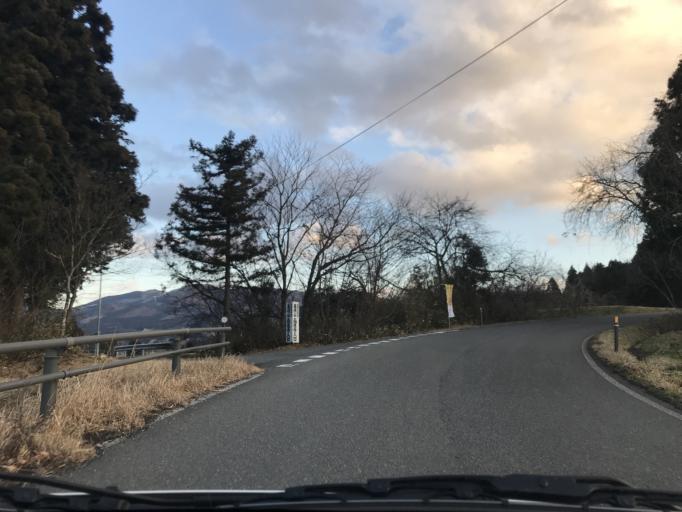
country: JP
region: Iwate
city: Mizusawa
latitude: 39.0331
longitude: 141.1192
